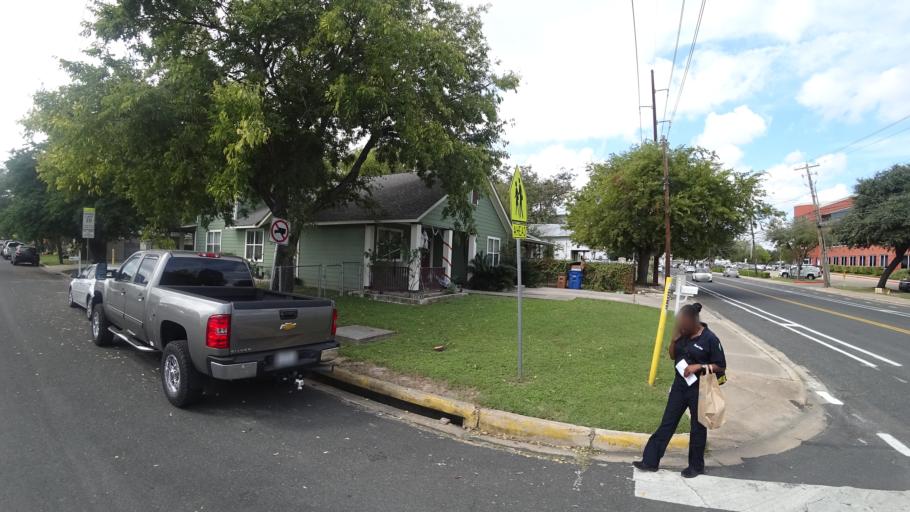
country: US
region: Texas
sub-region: Travis County
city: Austin
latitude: 30.2558
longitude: -97.7091
